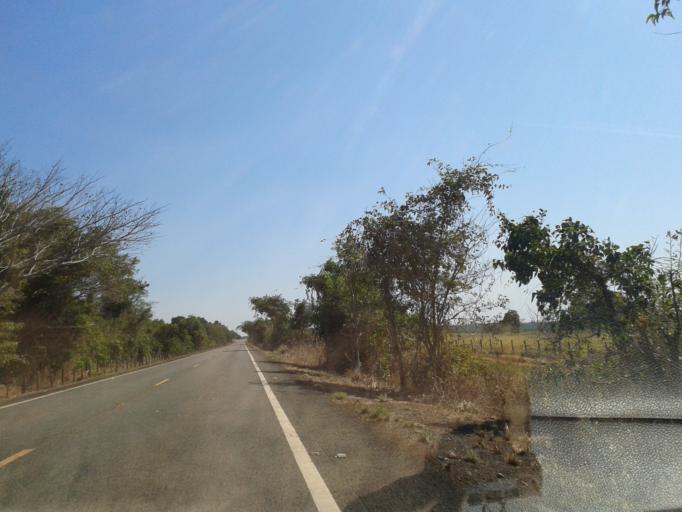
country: BR
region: Goias
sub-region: Sao Miguel Do Araguaia
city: Sao Miguel do Araguaia
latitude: -13.8978
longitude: -50.3271
